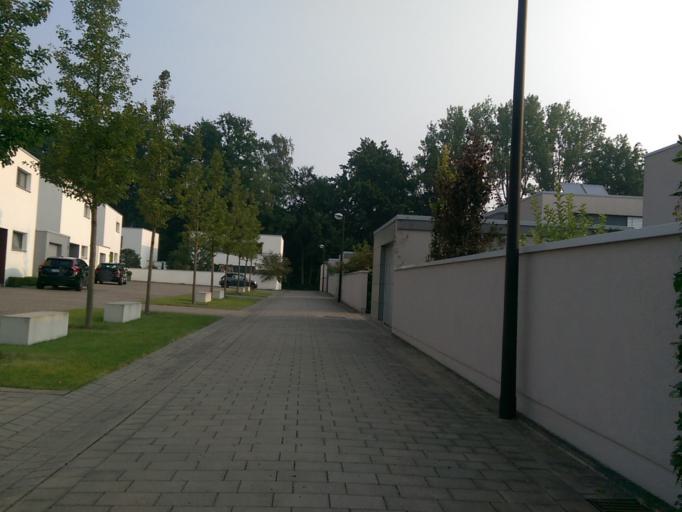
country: DE
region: North Rhine-Westphalia
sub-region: Regierungsbezirk Detmold
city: Guetersloh
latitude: 51.8995
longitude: 8.3510
